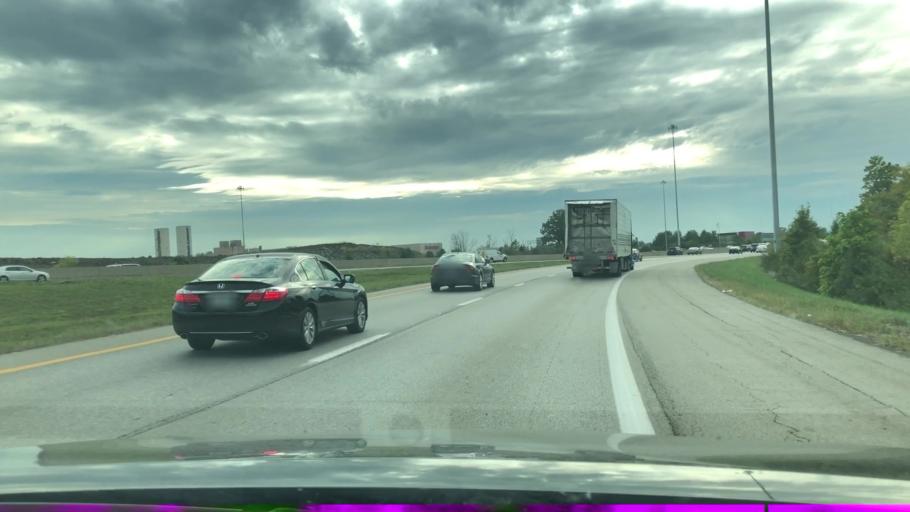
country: US
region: Ohio
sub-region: Franklin County
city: Worthington
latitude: 40.1111
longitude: -82.9817
